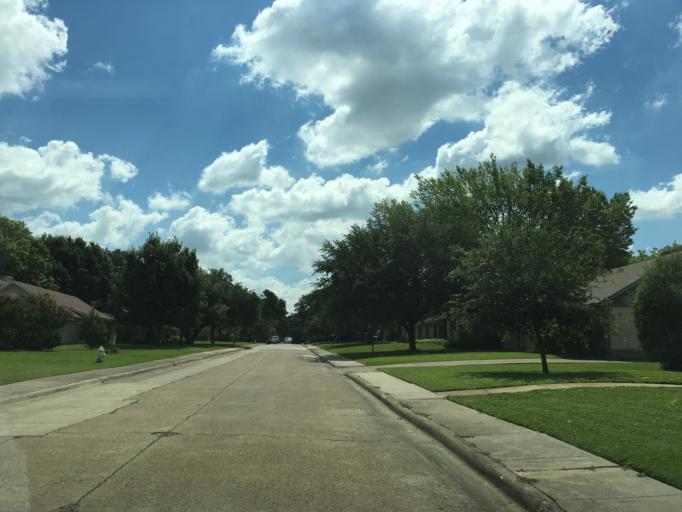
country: US
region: Texas
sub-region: Dallas County
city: Farmers Branch
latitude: 32.9209
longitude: -96.8591
